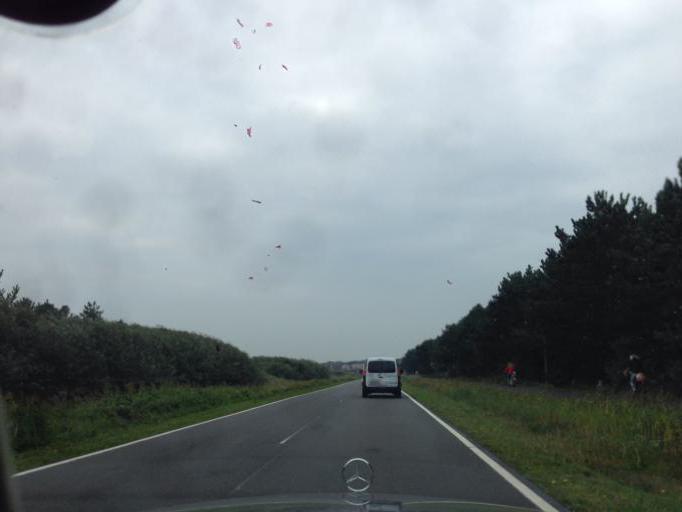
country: DE
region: Schleswig-Holstein
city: Westerland
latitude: 54.8569
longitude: 8.2926
